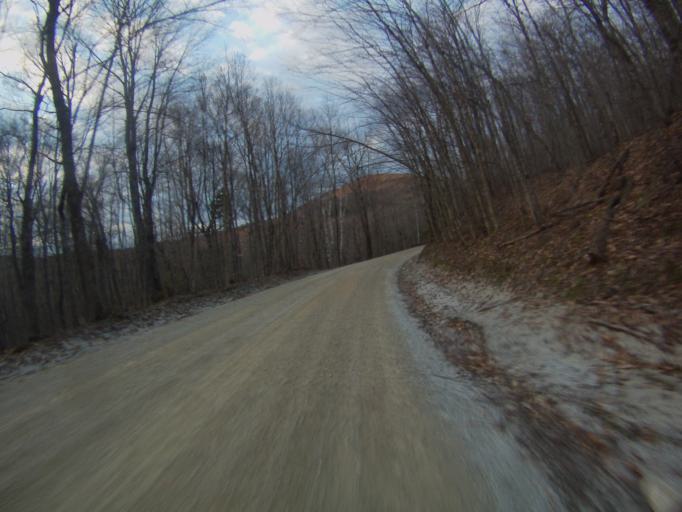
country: US
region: Vermont
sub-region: Rutland County
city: Brandon
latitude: 43.9137
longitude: -73.0189
